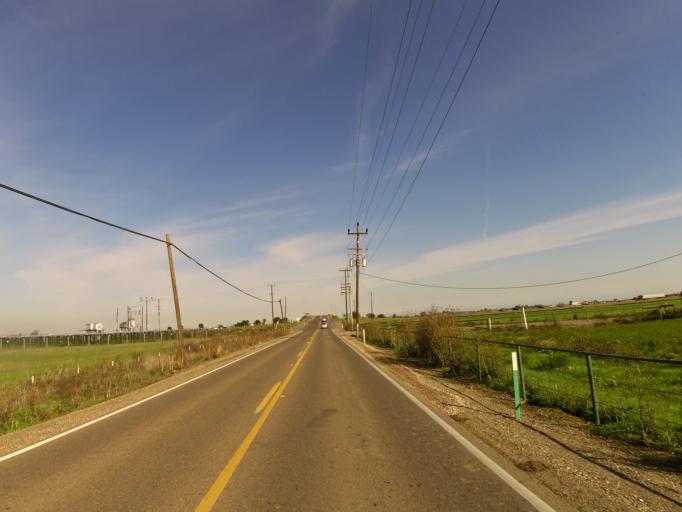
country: US
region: California
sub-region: Sacramento County
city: Walnut Grove
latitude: 38.2816
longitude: -121.4622
